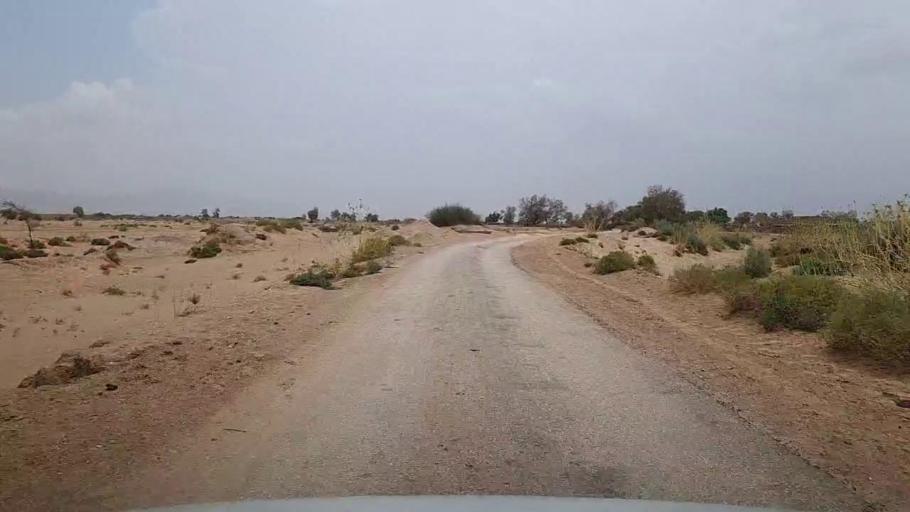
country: PK
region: Sindh
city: Sehwan
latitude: 26.3488
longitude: 67.7952
